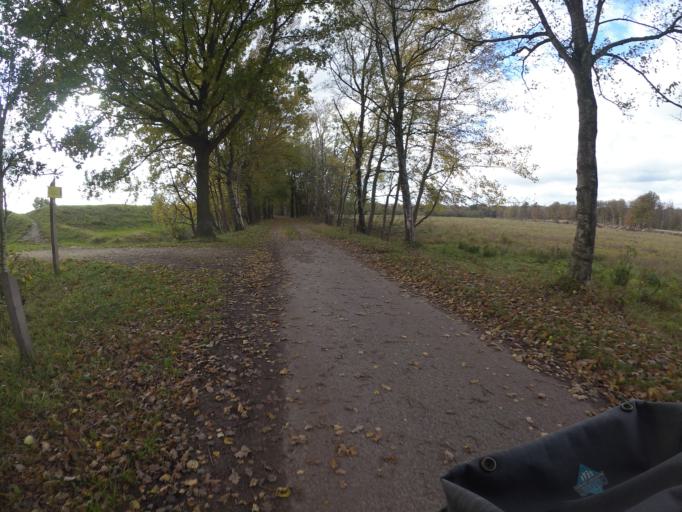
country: NL
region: North Brabant
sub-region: Gemeente Oirschot
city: Oirschot
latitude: 51.5550
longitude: 5.2808
